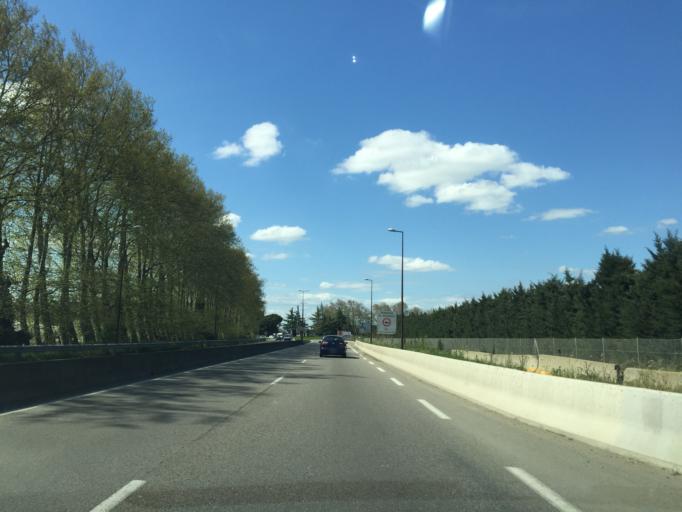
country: FR
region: Provence-Alpes-Cote d'Azur
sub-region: Departement du Vaucluse
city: Montfavet
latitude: 43.9139
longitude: 4.8778
